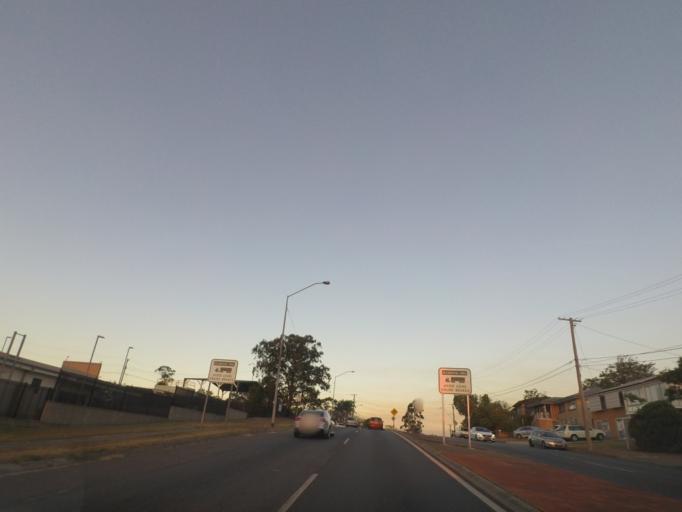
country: AU
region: Queensland
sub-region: Brisbane
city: Upper Mount Gravatt
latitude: -27.5555
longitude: 153.0907
